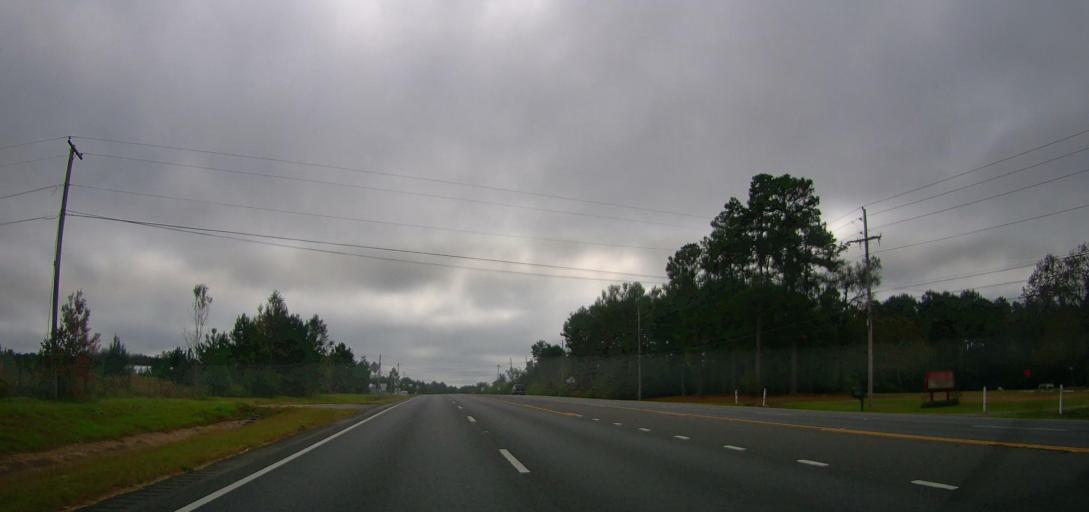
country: US
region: Georgia
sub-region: Thomas County
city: Thomasville
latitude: 30.8863
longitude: -83.9317
